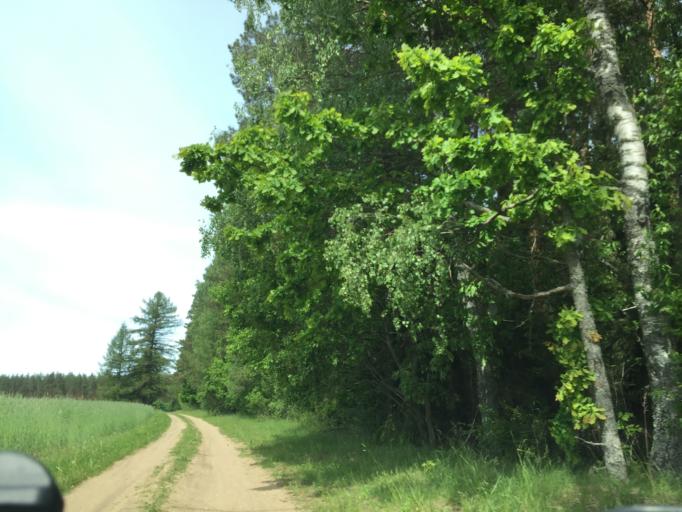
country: LV
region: Koceni
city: Koceni
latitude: 57.4436
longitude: 25.2823
